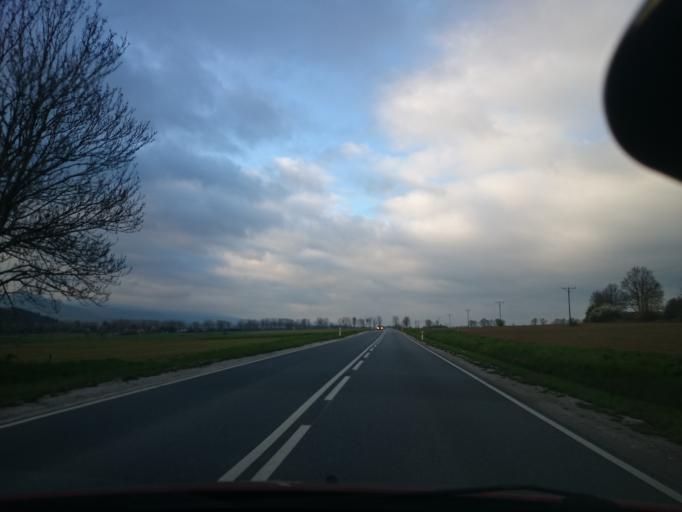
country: PL
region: Lower Silesian Voivodeship
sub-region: Powiat klodzki
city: Bystrzyca Klodzka
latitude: 50.3010
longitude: 16.6612
